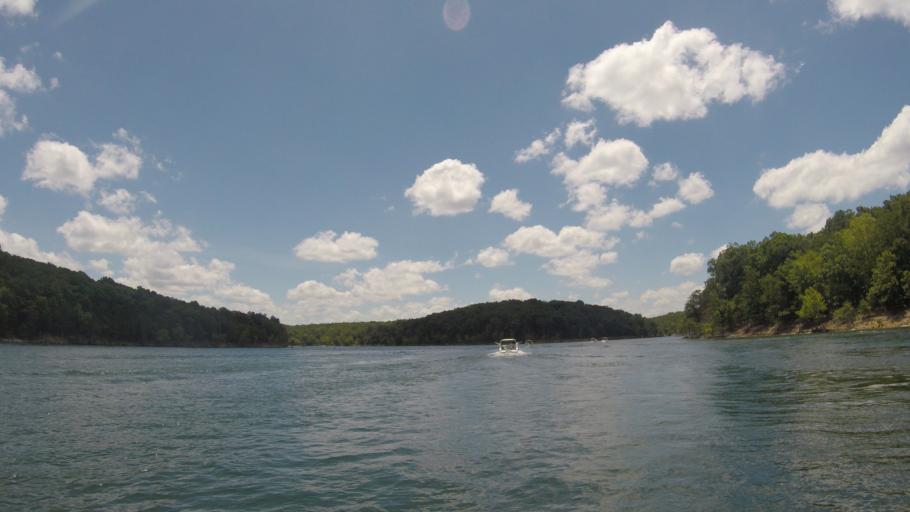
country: US
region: Missouri
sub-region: Barry County
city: Shell Knob
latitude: 36.5761
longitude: -93.5649
